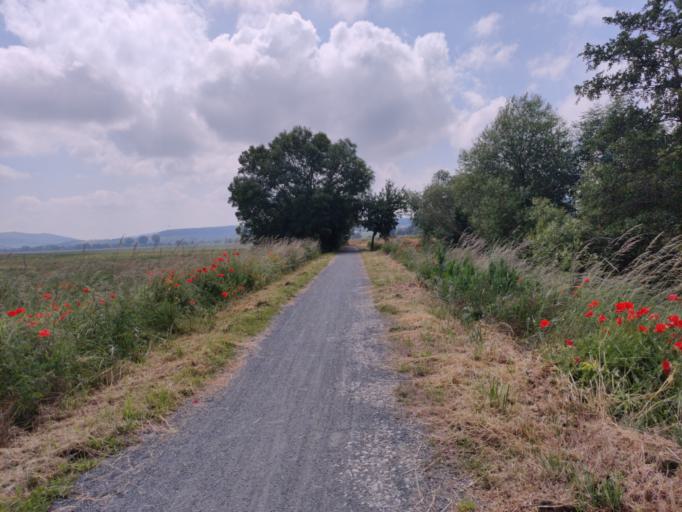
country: DE
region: Lower Saxony
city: Hildesheim
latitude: 52.1129
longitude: 9.9846
